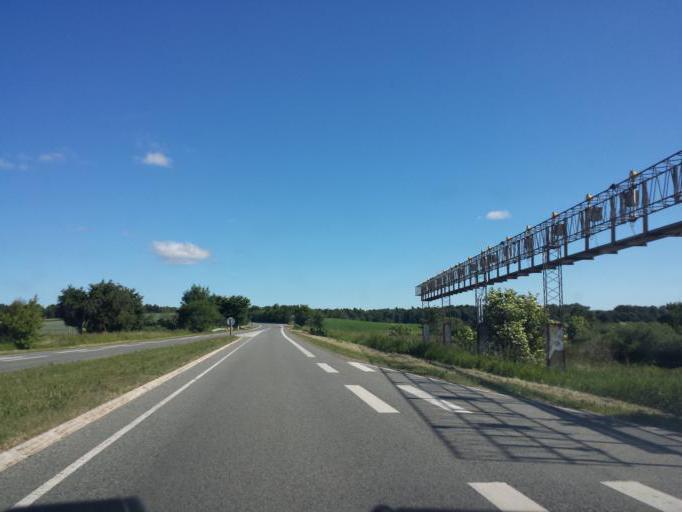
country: DK
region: Capital Region
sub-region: Egedal Kommune
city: Smorumnedre
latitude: 55.7720
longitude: 12.2928
